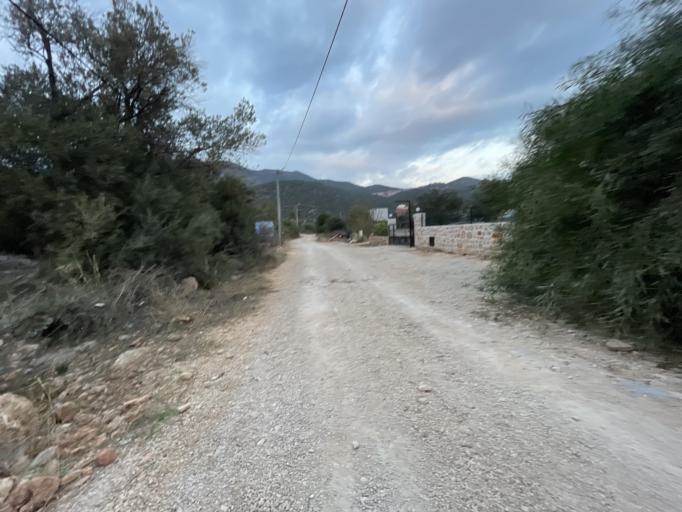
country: TR
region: Antalya
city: Kas
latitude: 36.1873
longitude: 29.6528
